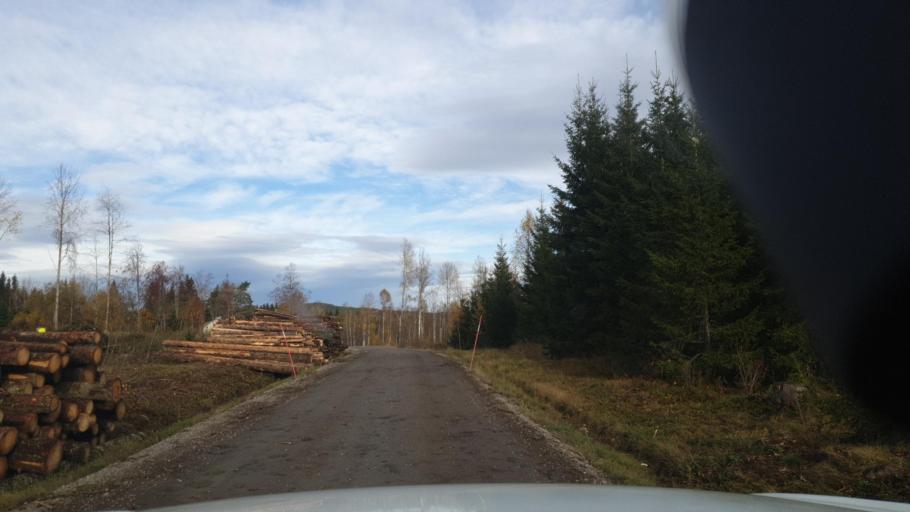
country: SE
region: Vaermland
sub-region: Eda Kommun
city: Amotfors
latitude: 59.8605
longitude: 12.5092
